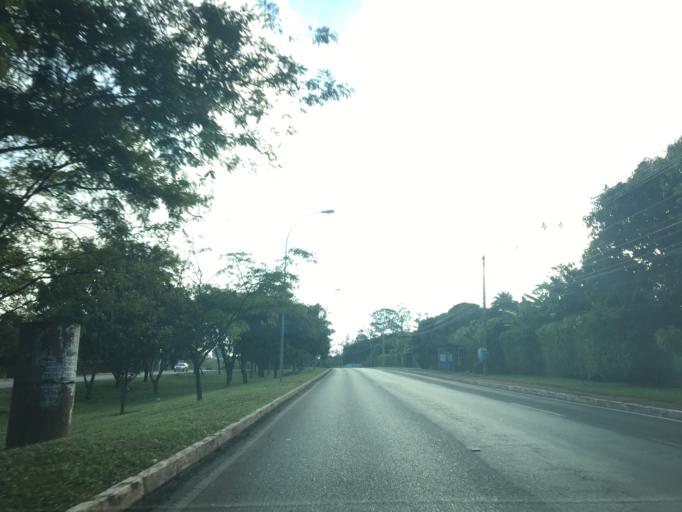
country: BR
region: Federal District
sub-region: Brasilia
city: Brasilia
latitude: -15.8265
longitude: -47.8075
